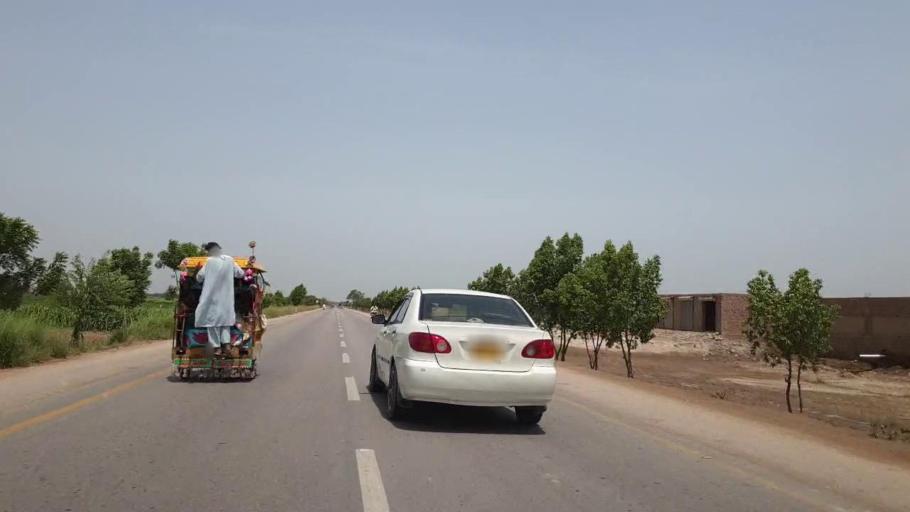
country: PK
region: Sindh
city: Nawabshah
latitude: 26.2322
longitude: 68.4830
